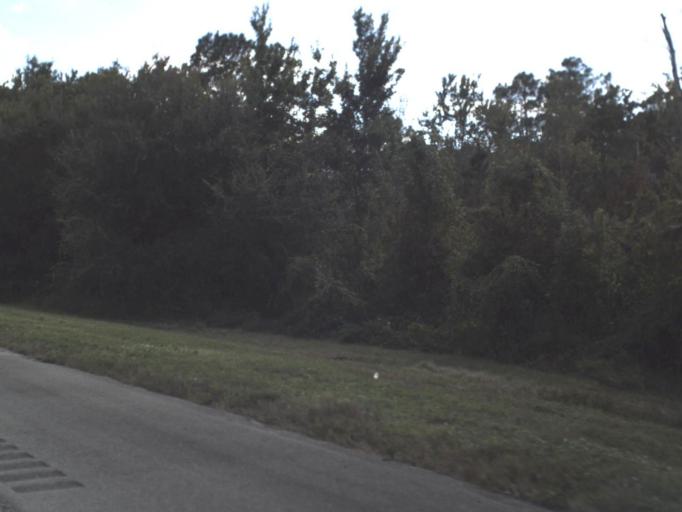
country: US
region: Florida
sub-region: Indian River County
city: Fellsmere
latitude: 27.6357
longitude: -80.8482
